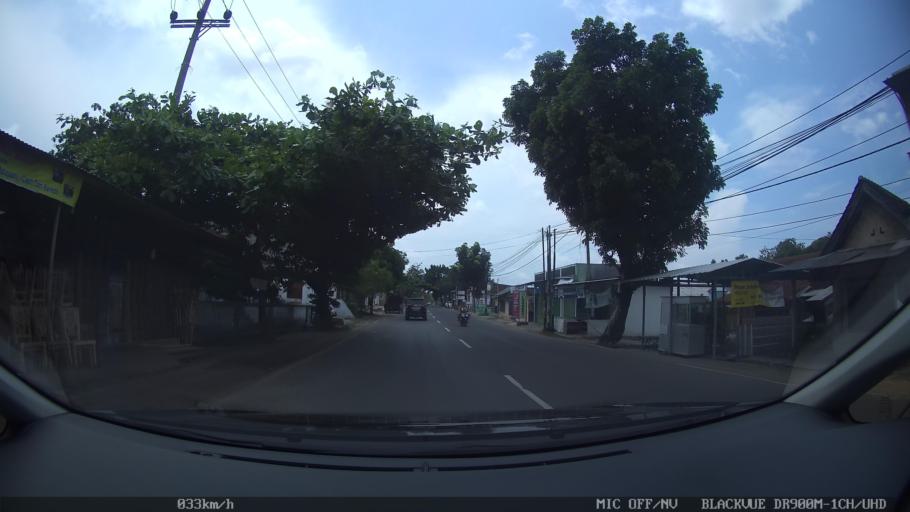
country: ID
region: Lampung
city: Bandarlampung
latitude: -5.4042
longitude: 105.2421
